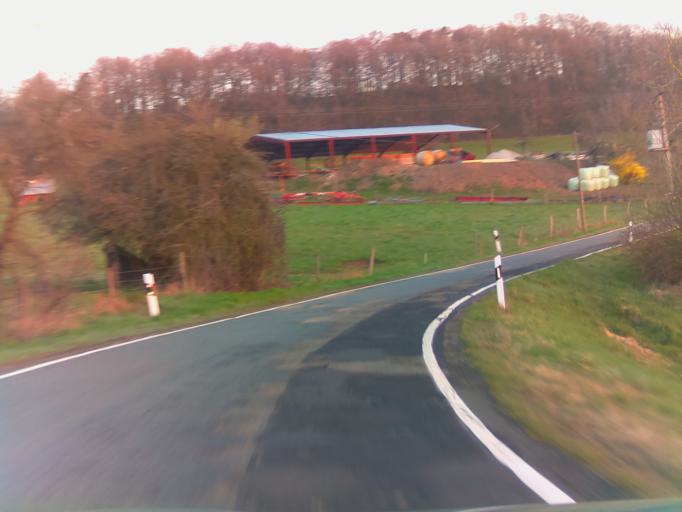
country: DE
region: Rheinland-Pfalz
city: Kirrweiler
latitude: 49.6429
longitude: 7.5002
